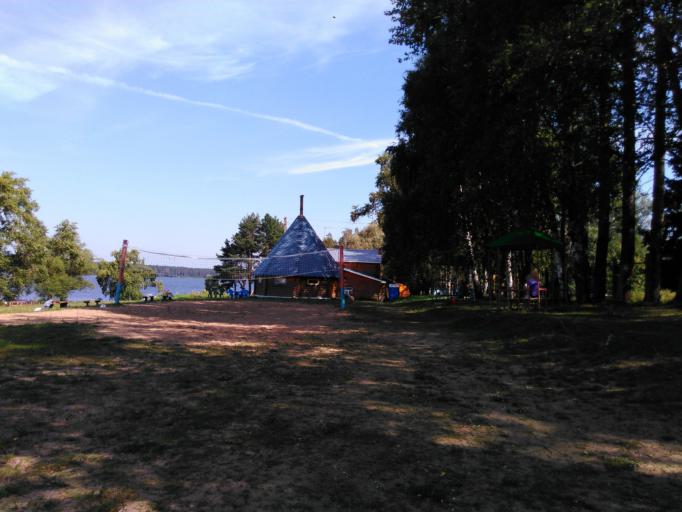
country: RU
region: Tverskaya
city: Konakovo
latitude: 56.6838
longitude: 36.6938
